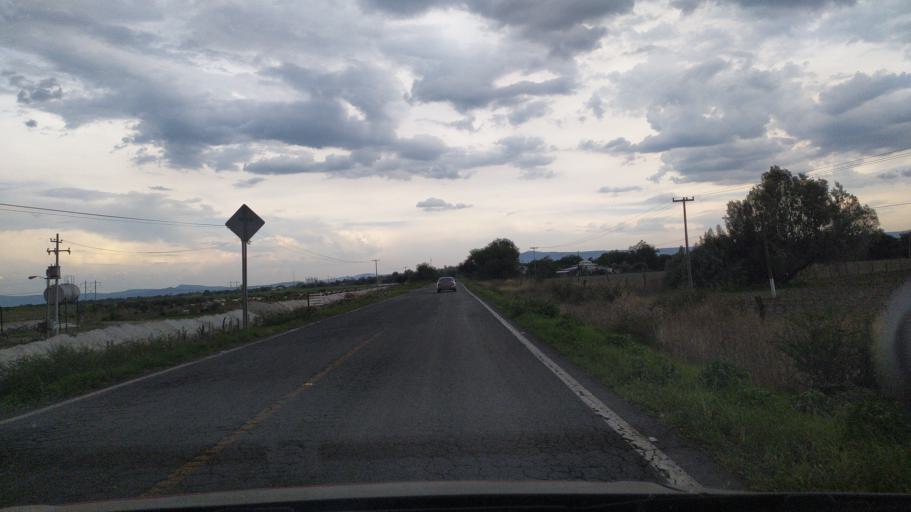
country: MX
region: Guanajuato
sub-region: San Francisco del Rincon
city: San Ignacio de Hidalgo
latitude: 20.8360
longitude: -101.9003
